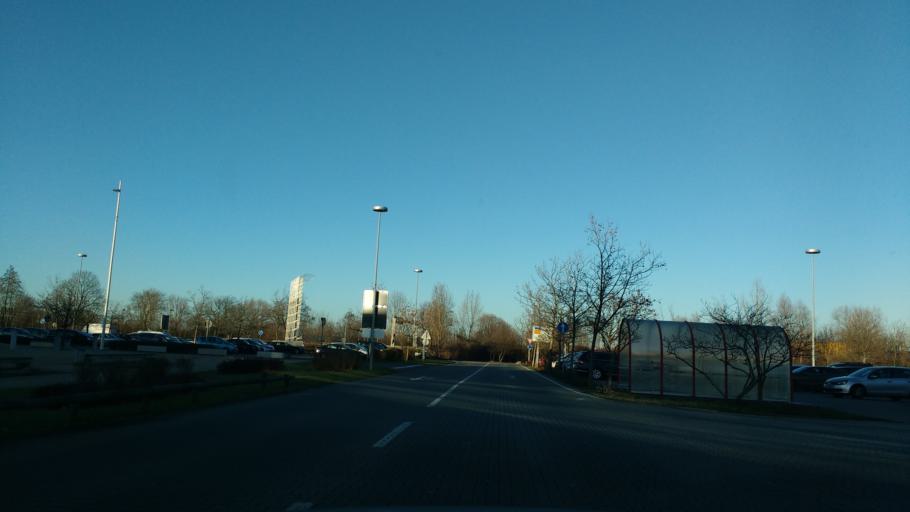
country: DE
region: Saxony-Anhalt
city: Gunthersdorf
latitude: 51.3455
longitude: 12.1806
